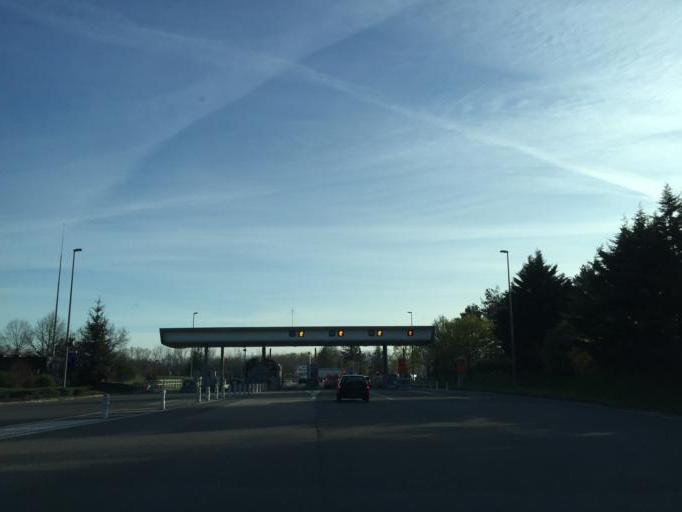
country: FR
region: Rhone-Alpes
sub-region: Departement de la Loire
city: Feurs
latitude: 45.7370
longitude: 4.1856
